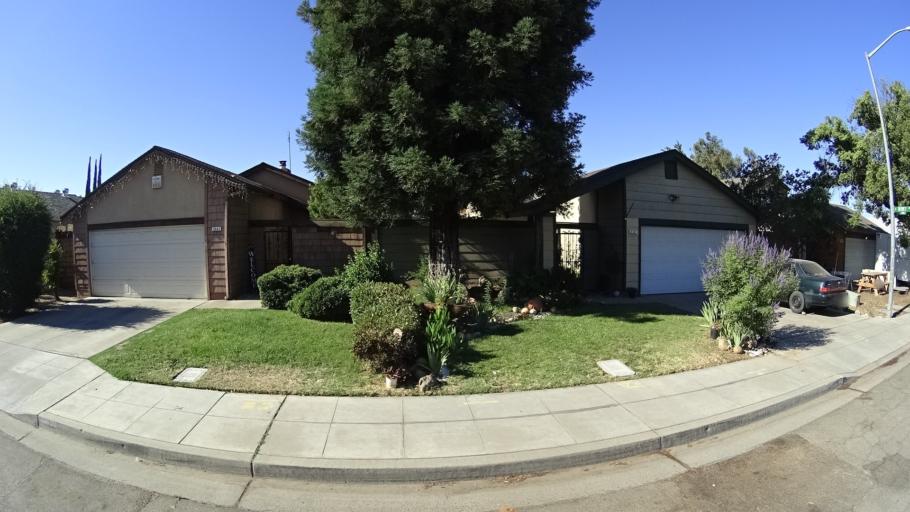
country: US
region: California
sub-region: Fresno County
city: West Park
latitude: 36.7780
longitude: -119.8567
